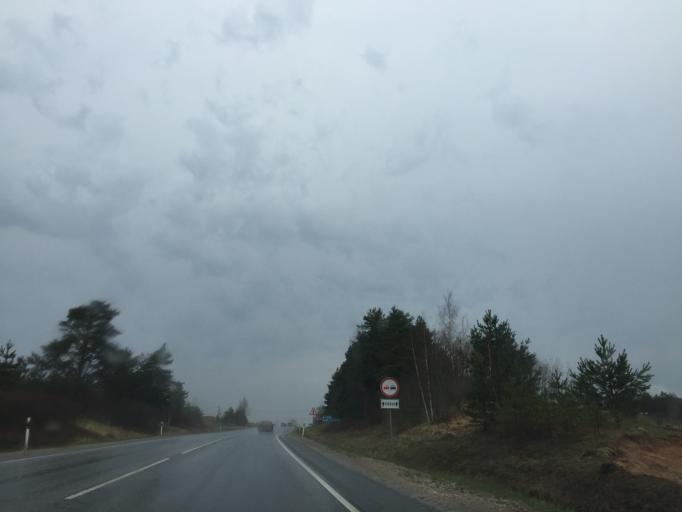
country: EE
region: Tartu
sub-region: UElenurme vald
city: Ulenurme
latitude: 58.2561
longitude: 26.6822
